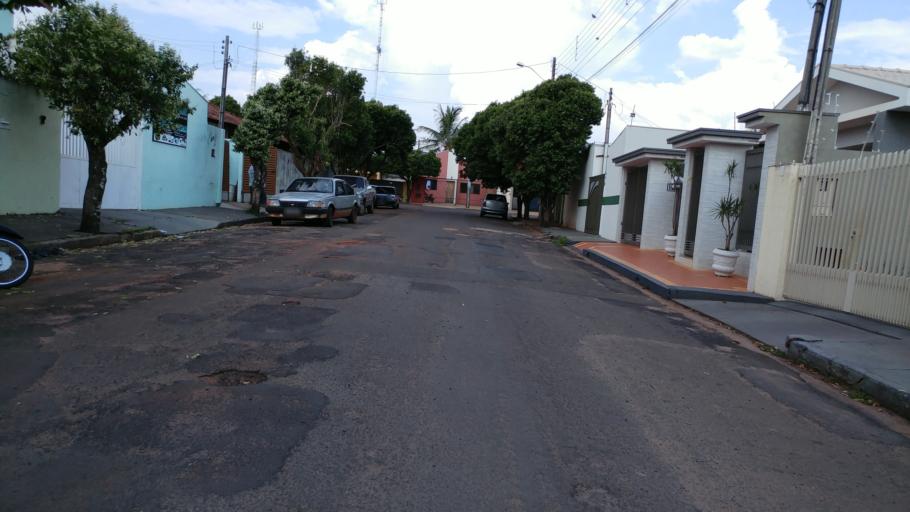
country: BR
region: Sao Paulo
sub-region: Paraguacu Paulista
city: Paraguacu Paulista
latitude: -22.4203
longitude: -50.5849
